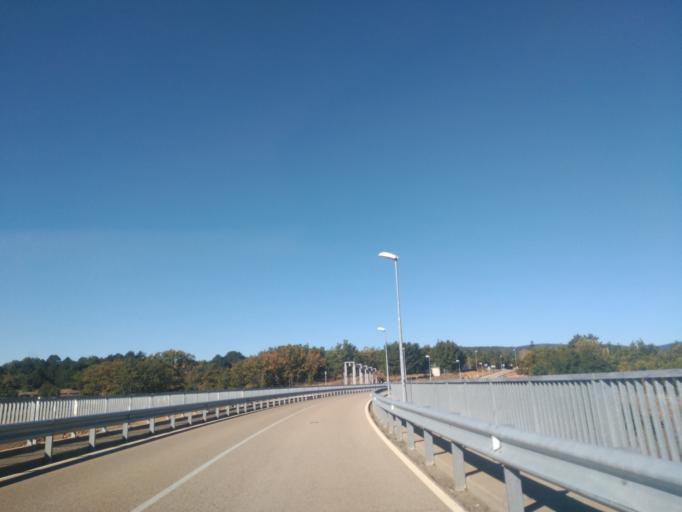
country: ES
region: Castille and Leon
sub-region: Provincia de Soria
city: Vinuesa
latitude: 41.8758
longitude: -2.7042
